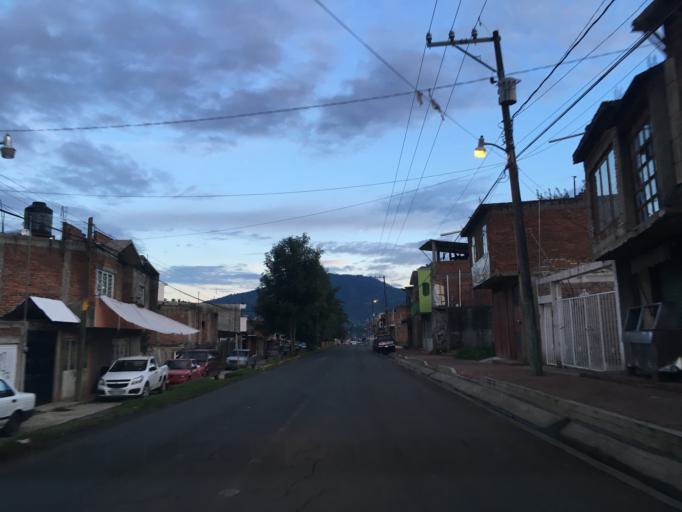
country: MX
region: Michoacan
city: Cheran
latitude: 19.6784
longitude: -101.9535
